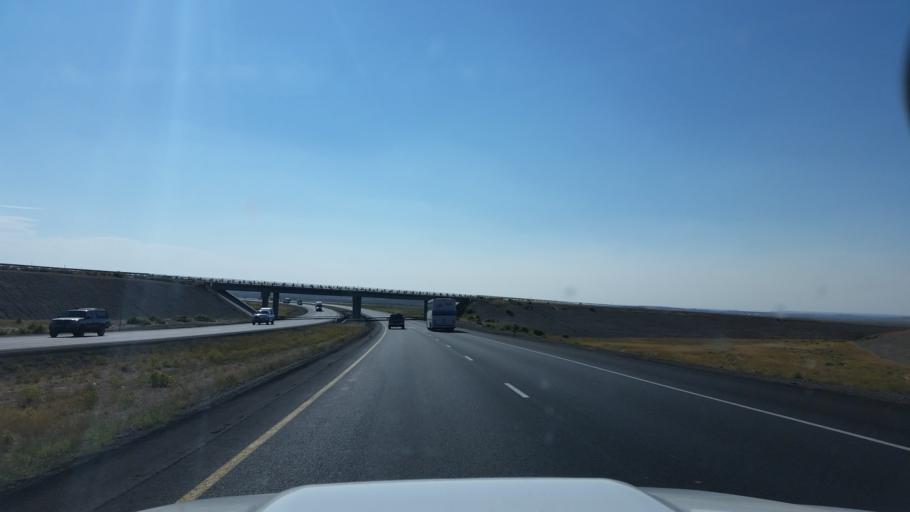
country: US
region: Wyoming
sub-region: Uinta County
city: Lyman
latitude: 41.5445
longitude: -109.9083
